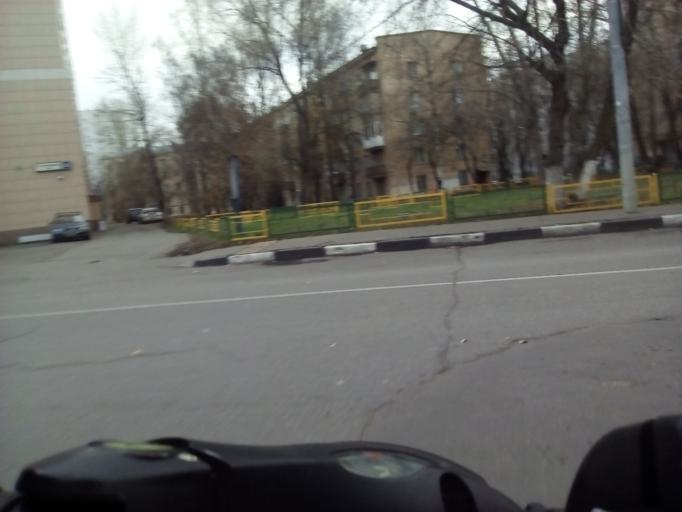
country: RU
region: Moscow
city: Lefortovo
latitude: 55.7662
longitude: 37.7132
